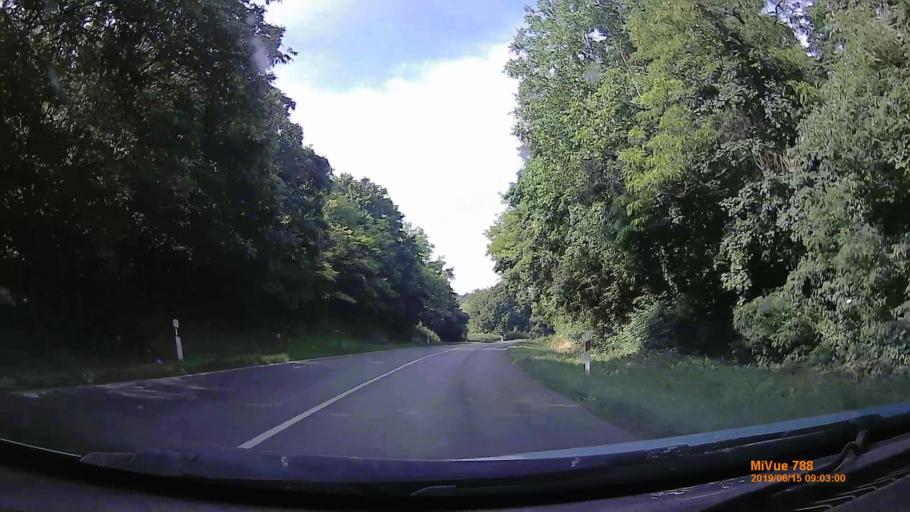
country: HU
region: Tolna
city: Iregszemcse
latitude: 46.7499
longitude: 18.1659
